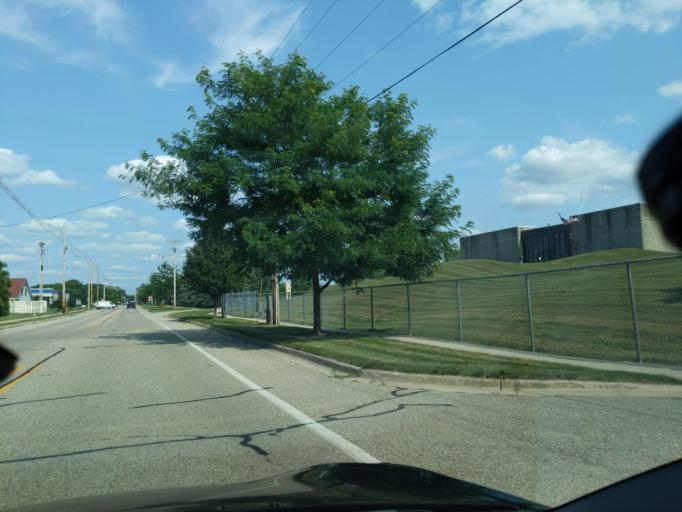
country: US
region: Michigan
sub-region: Kent County
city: Lowell
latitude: 42.9292
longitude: -85.3576
